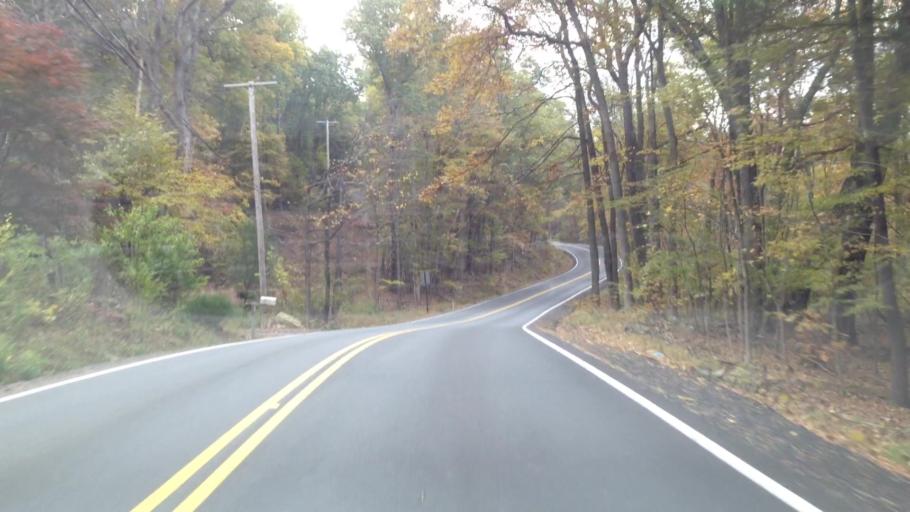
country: US
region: New York
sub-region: Ulster County
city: Tillson
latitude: 41.8240
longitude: -74.0032
